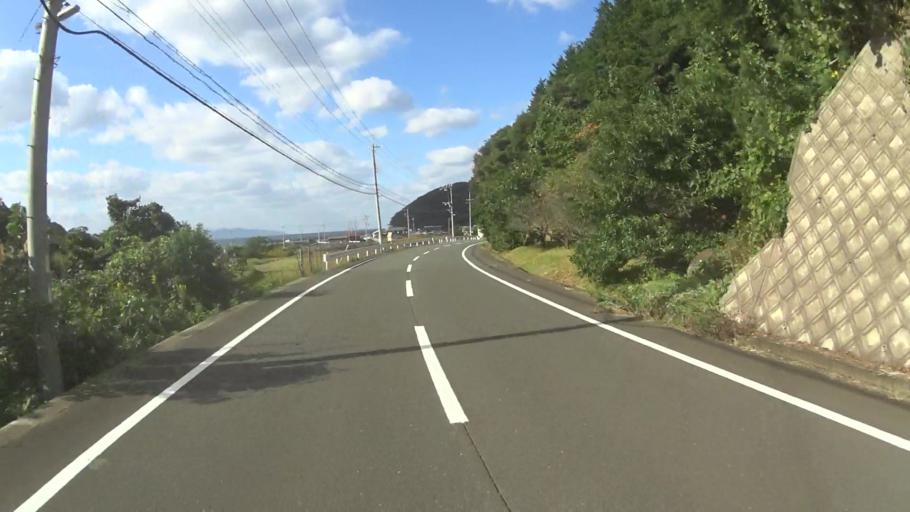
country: JP
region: Kyoto
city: Maizuru
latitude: 35.5634
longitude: 135.4272
